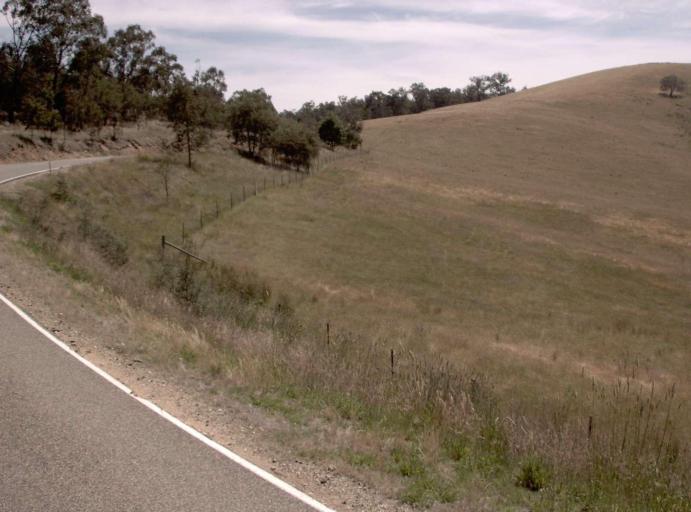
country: AU
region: Victoria
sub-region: Alpine
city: Mount Beauty
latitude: -37.0538
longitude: 147.6167
